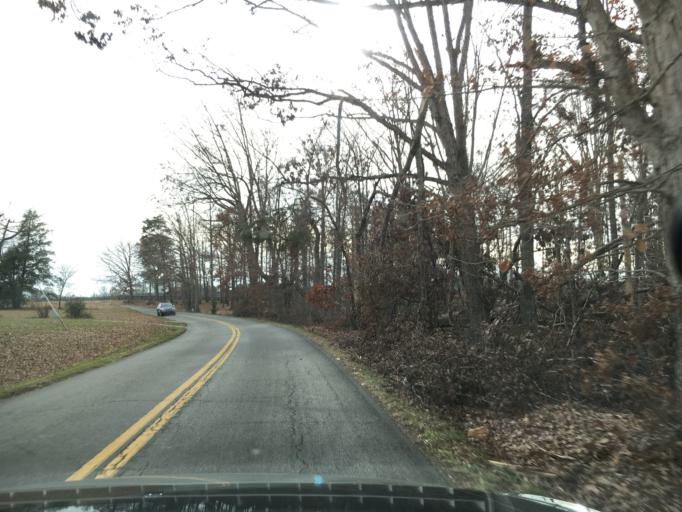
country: US
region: Virginia
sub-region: Henrico County
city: Wyndham
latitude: 37.7152
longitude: -77.6842
